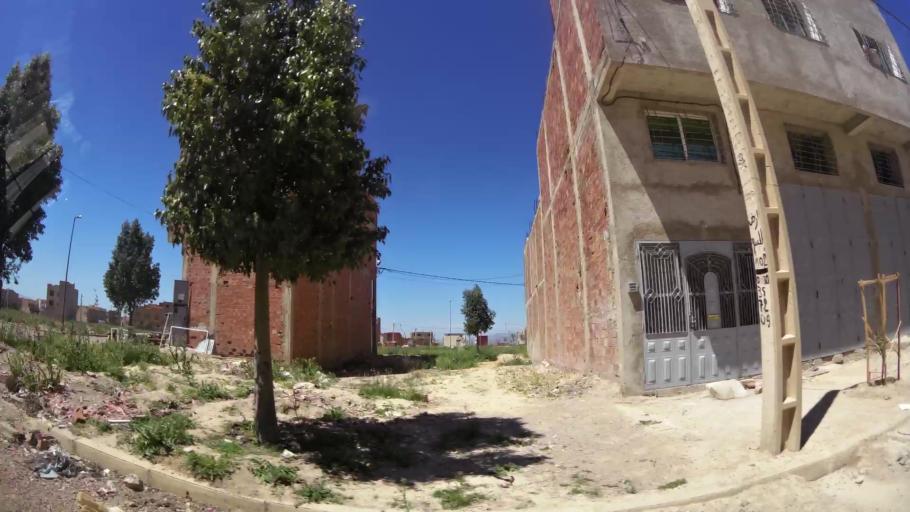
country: MA
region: Oriental
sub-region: Oujda-Angad
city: Oujda
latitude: 34.6826
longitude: -1.8644
